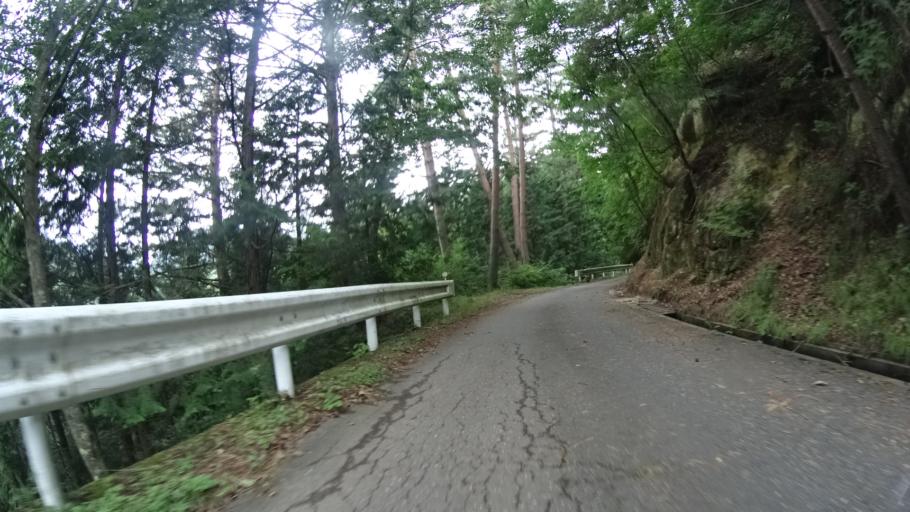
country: JP
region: Yamanashi
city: Kofu-shi
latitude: 35.8119
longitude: 138.5946
